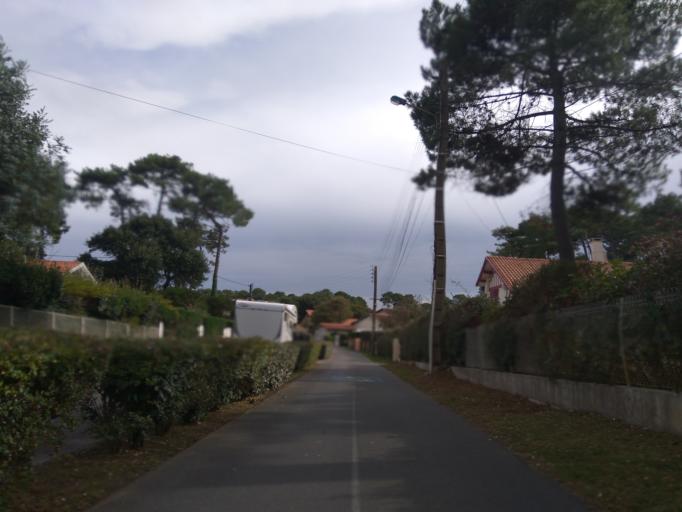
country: FR
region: Aquitaine
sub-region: Departement des Landes
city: Capbreton
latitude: 43.6404
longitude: -1.4405
